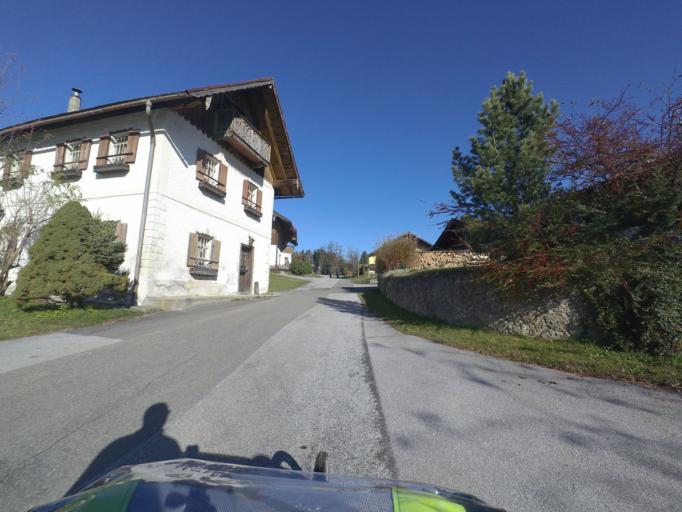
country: AT
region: Salzburg
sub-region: Politischer Bezirk Hallein
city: Adnet
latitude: 47.6700
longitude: 13.1440
